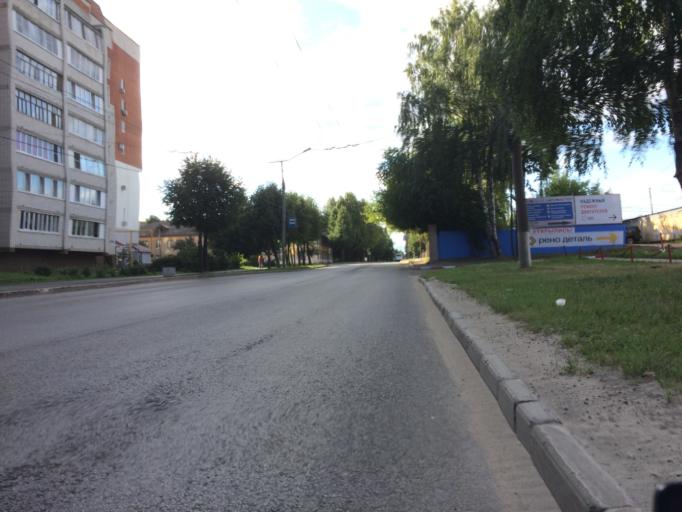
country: RU
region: Mariy-El
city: Yoshkar-Ola
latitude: 56.6397
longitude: 47.8600
